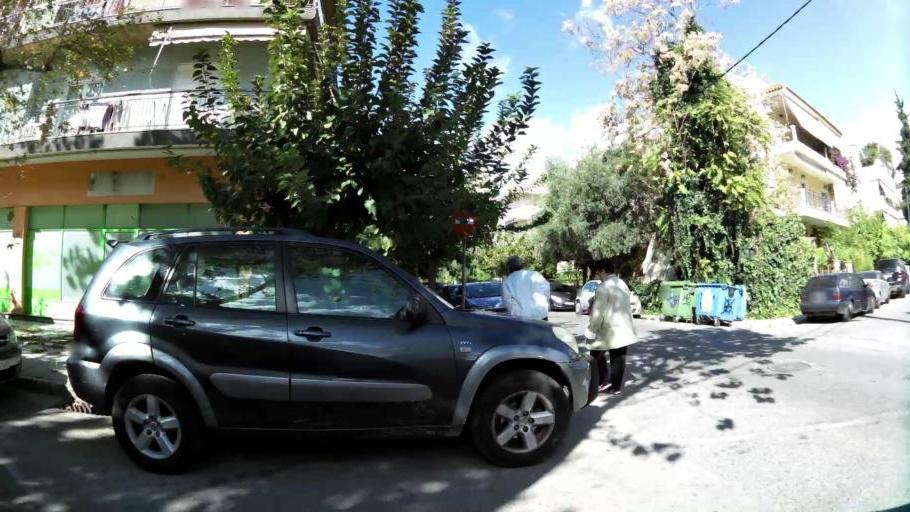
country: GR
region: Attica
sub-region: Nomarchia Athinas
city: Neo Psychiko
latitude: 38.0057
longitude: 23.7875
